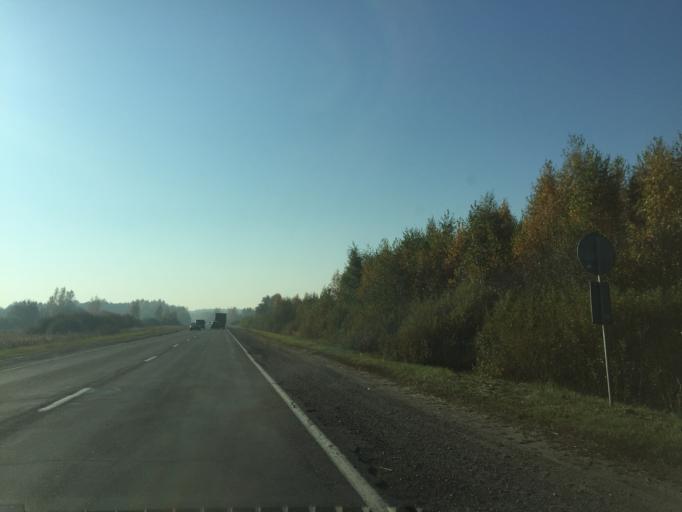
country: BY
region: Gomel
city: Kastsyukowka
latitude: 52.4477
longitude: 30.8247
